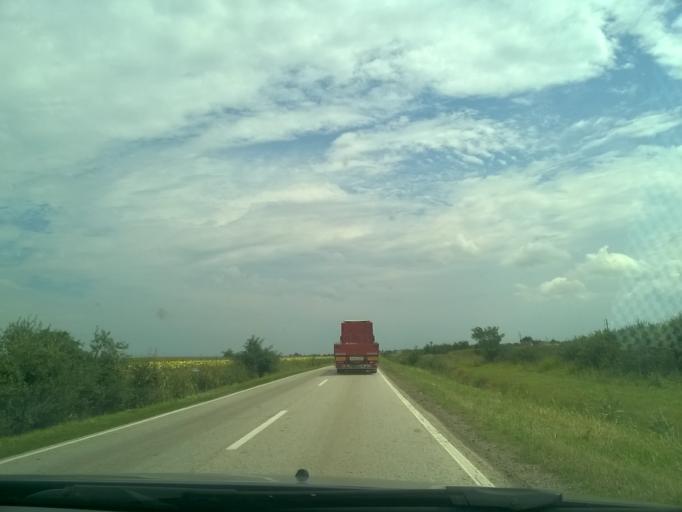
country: RS
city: Lazarevo
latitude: 45.3888
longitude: 20.5156
